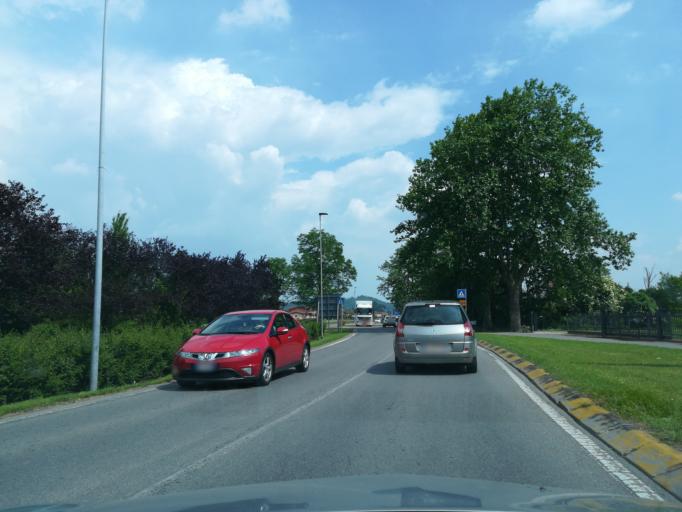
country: IT
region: Lombardy
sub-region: Provincia di Bergamo
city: Brusaporto
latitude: 45.6770
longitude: 9.7480
